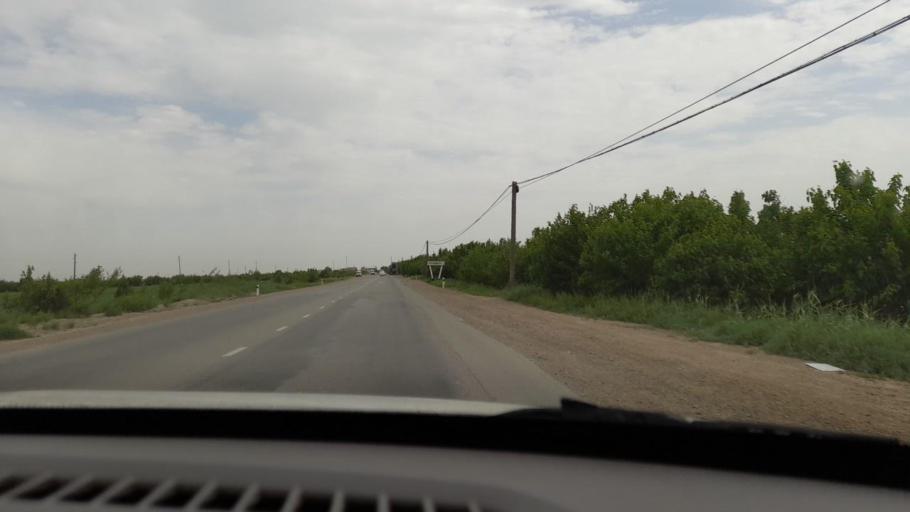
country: UZ
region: Bukhara
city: Romiton
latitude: 39.9434
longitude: 64.3568
